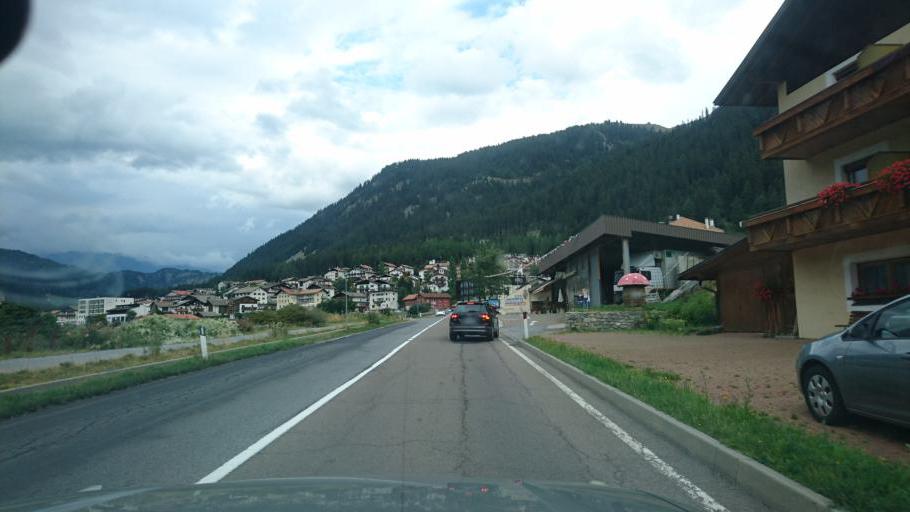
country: IT
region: Trentino-Alto Adige
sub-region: Bolzano
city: Curon Venosta
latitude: 46.8253
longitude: 10.5215
